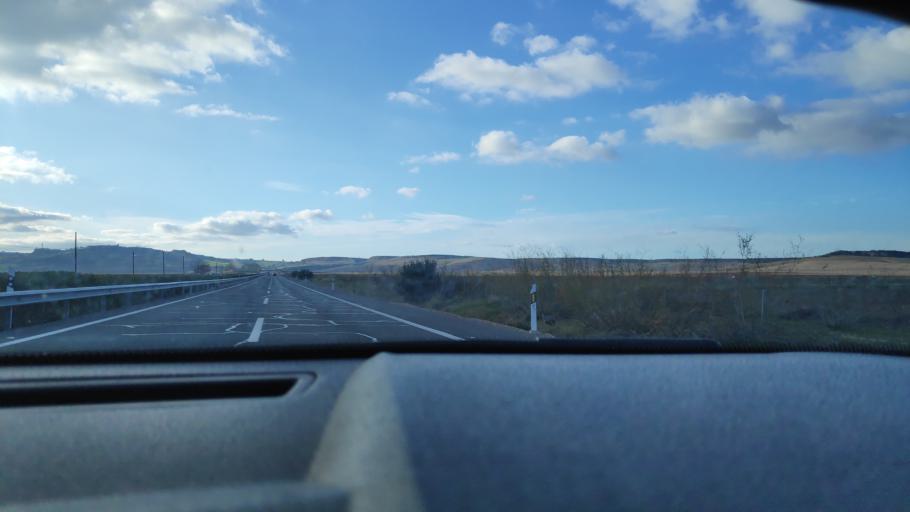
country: ES
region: Andalusia
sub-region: Provincia de Sevilla
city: Carmona
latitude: 37.4797
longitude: -5.5796
